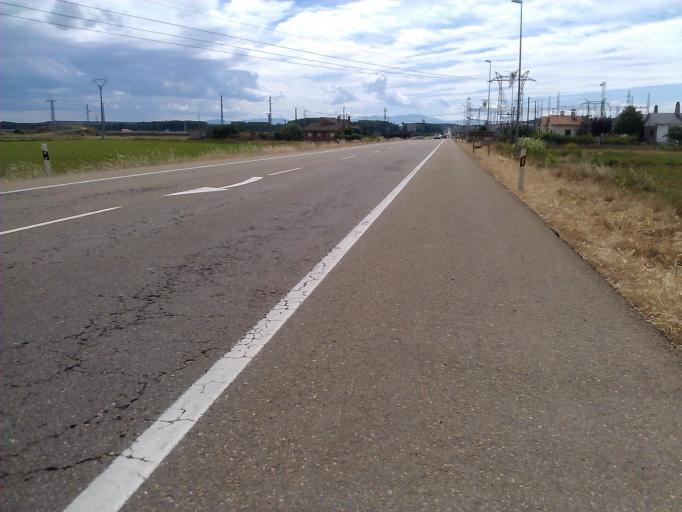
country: ES
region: Castille and Leon
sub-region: Provincia de Leon
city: Hospital de Orbigo
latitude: 42.4576
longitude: -5.8891
